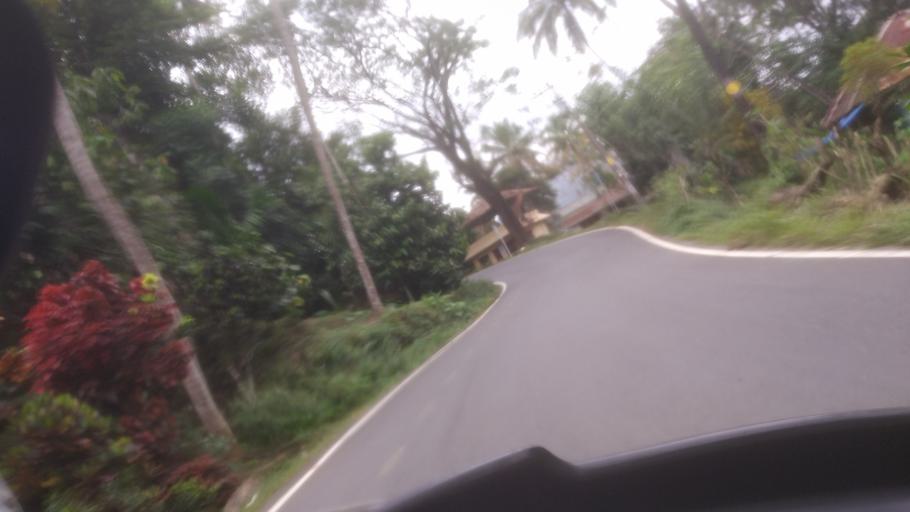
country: IN
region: Kerala
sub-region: Idukki
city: Idukki
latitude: 9.9653
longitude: 77.0054
